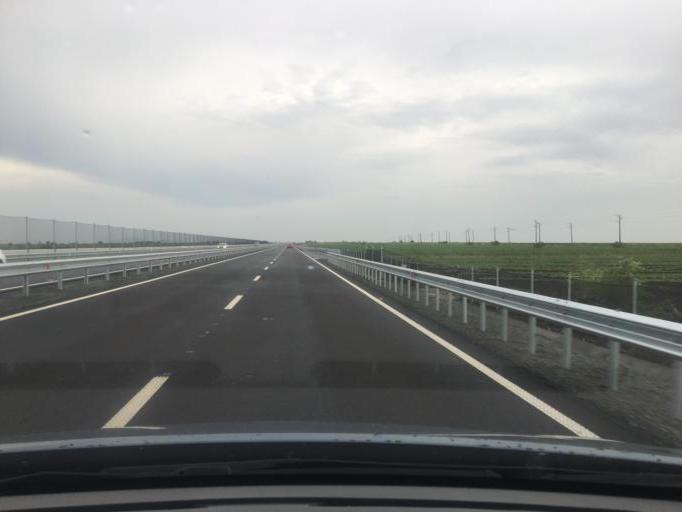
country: BG
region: Burgas
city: Aheloy
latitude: 42.6116
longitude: 27.6226
